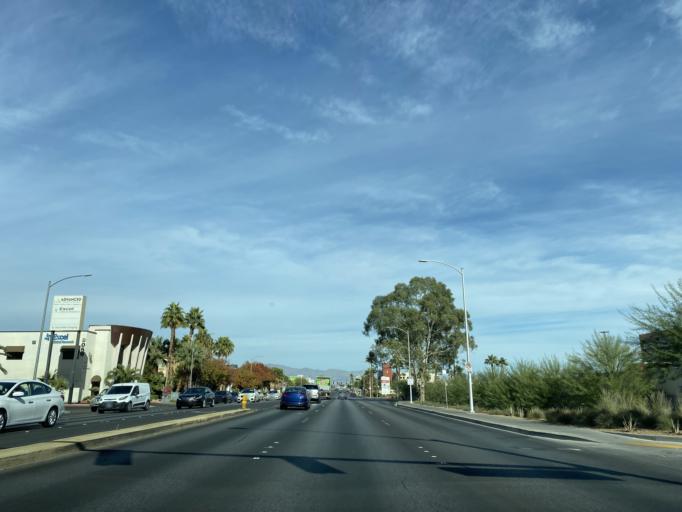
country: US
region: Nevada
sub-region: Clark County
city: Winchester
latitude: 36.1338
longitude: -115.1368
